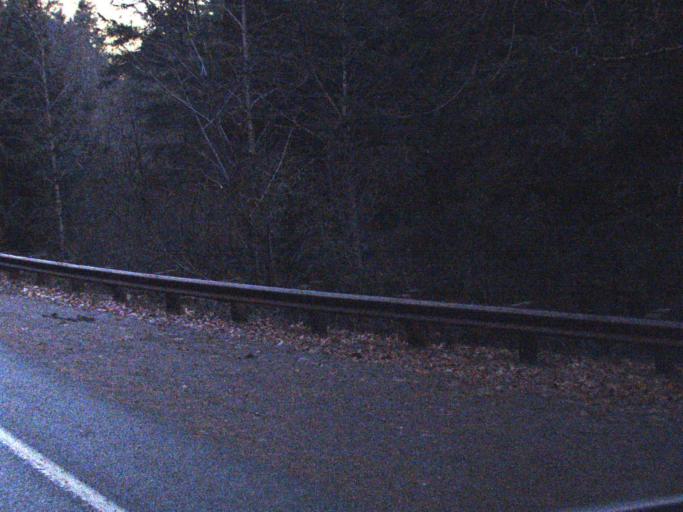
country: US
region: Washington
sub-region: Snohomish County
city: Darrington
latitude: 48.7104
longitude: -121.1470
